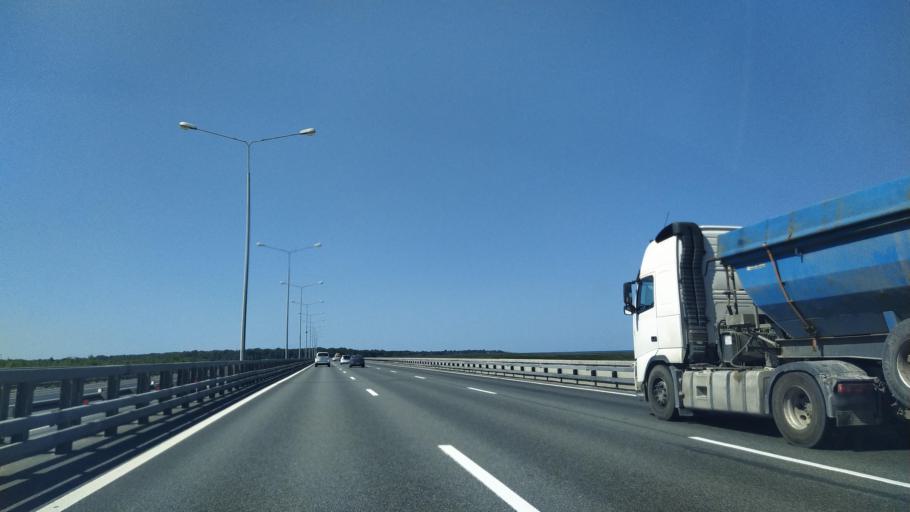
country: RU
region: St.-Petersburg
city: Kronshtadt
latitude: 60.0211
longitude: 29.7482
